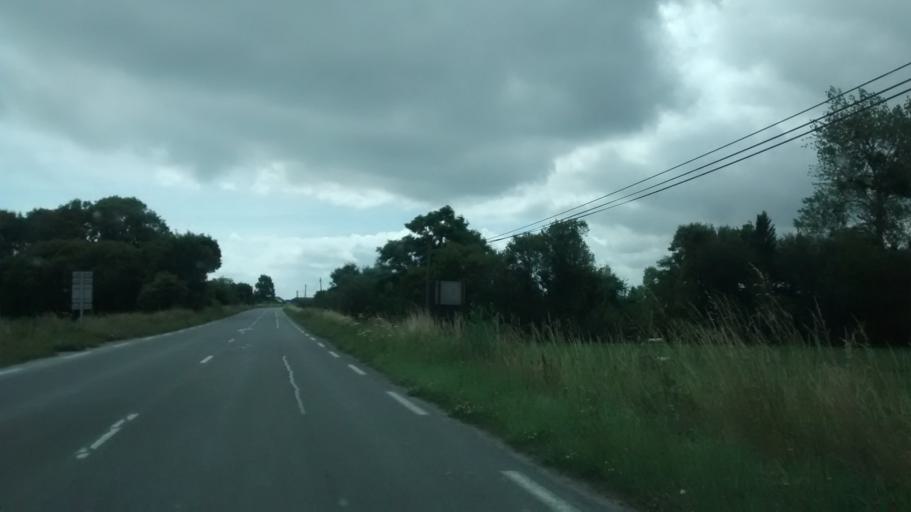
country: FR
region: Brittany
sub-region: Departement d'Ille-et-Vilaine
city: Saint-Meloir-des-Ondes
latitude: 48.6402
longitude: -1.8733
